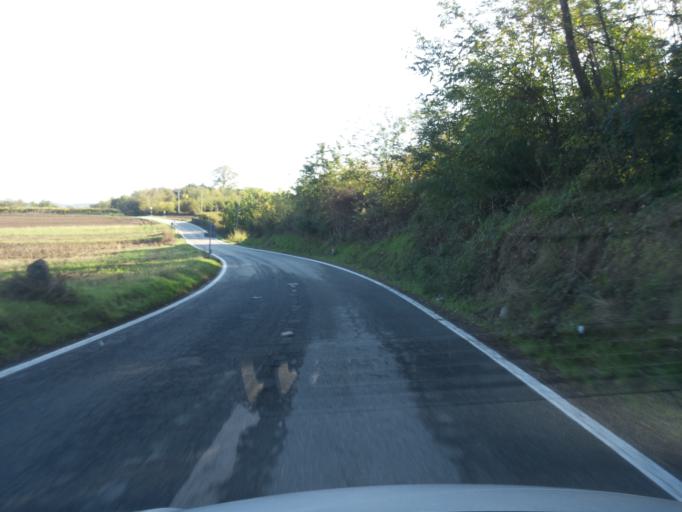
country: IT
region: Piedmont
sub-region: Provincia di Torino
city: Vische
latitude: 45.3191
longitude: 7.9367
